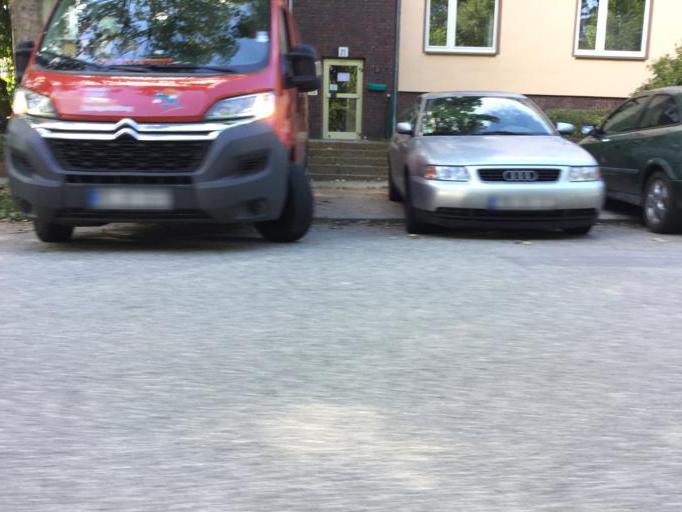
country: DE
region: Hamburg
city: Alsterdorf
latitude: 53.6177
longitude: 10.0098
